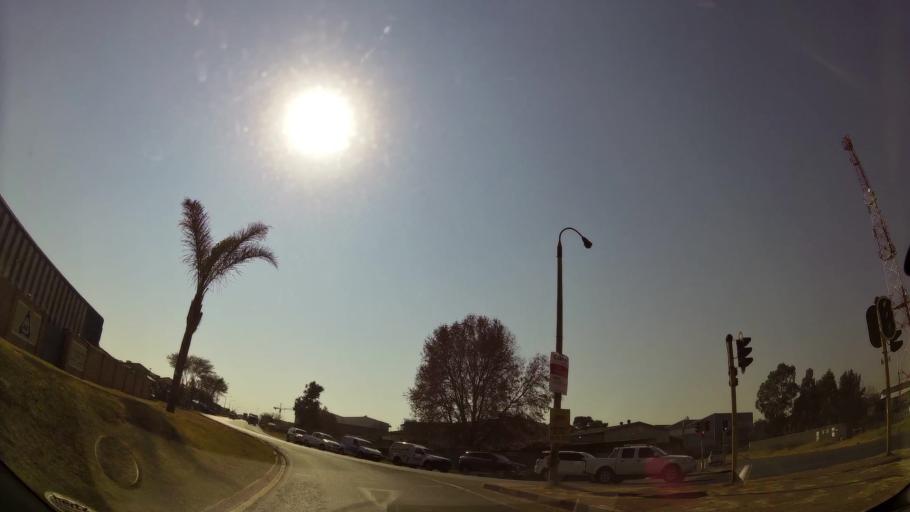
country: ZA
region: Gauteng
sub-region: Ekurhuleni Metropolitan Municipality
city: Boksburg
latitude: -26.1577
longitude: 28.2201
